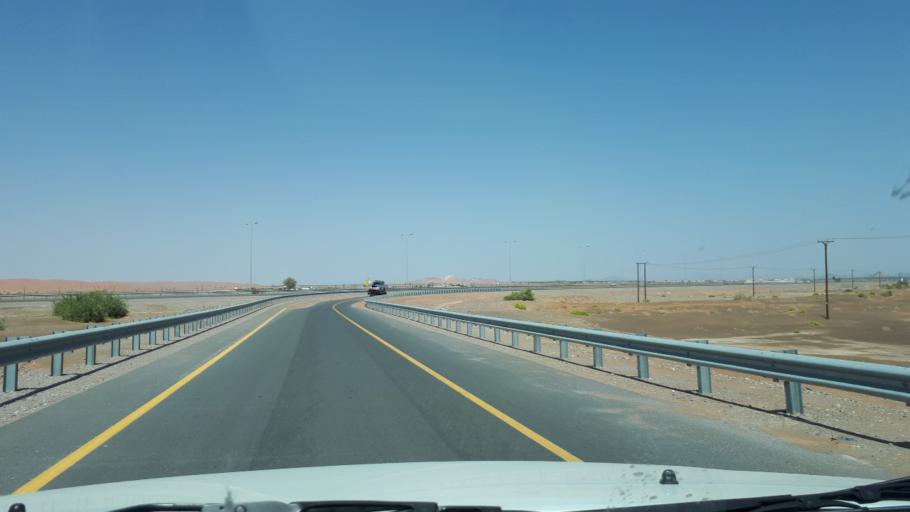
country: OM
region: Ash Sharqiyah
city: Al Qabil
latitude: 22.5251
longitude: 58.7418
